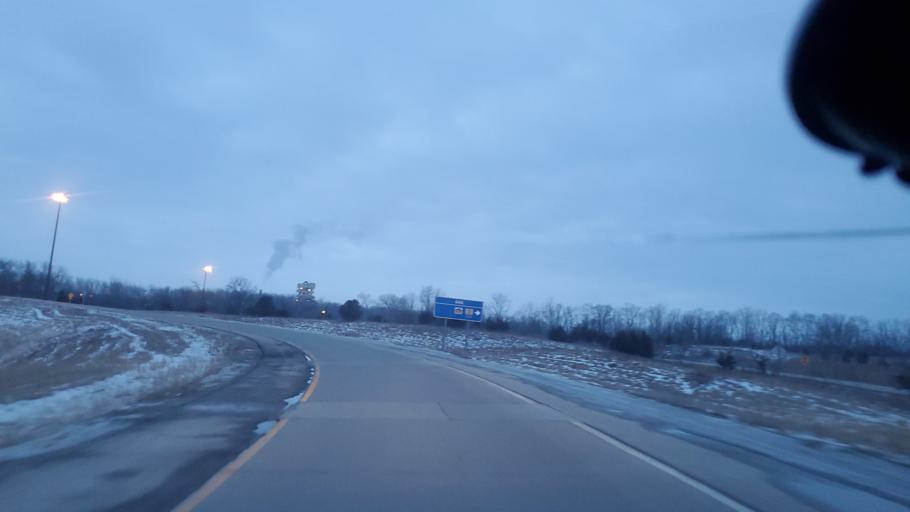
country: US
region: Illinois
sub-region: LaSalle County
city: La Salle
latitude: 41.3374
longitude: -89.0728
